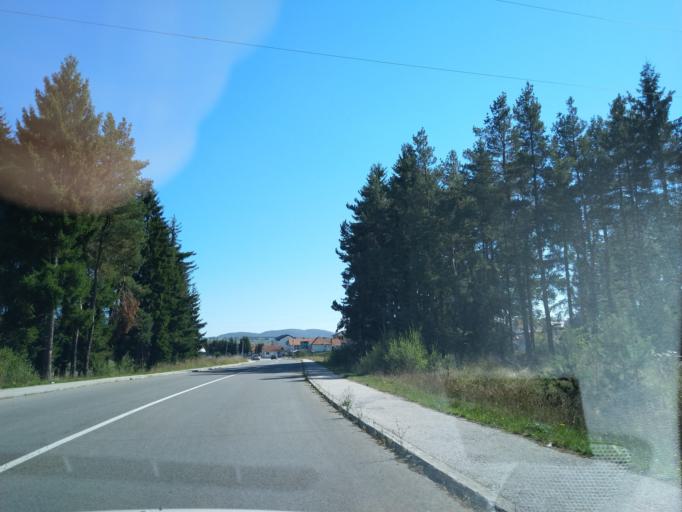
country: RS
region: Central Serbia
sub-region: Zlatiborski Okrug
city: Sjenica
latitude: 43.2719
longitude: 20.0180
